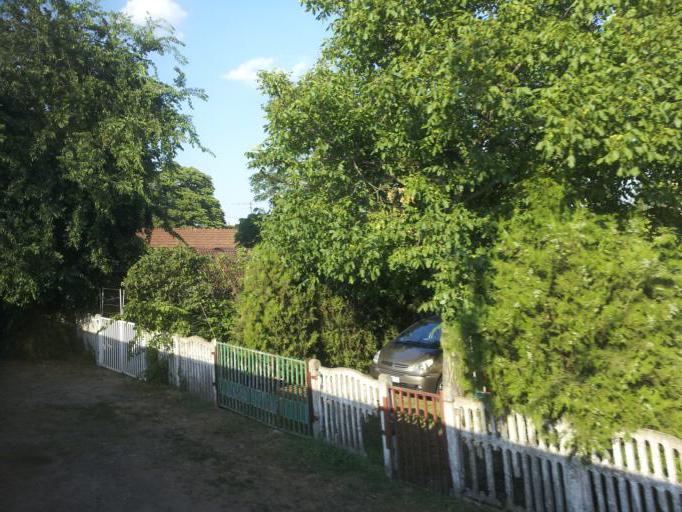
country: HU
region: Pest
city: Dunaharaszti
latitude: 47.3522
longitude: 19.0965
